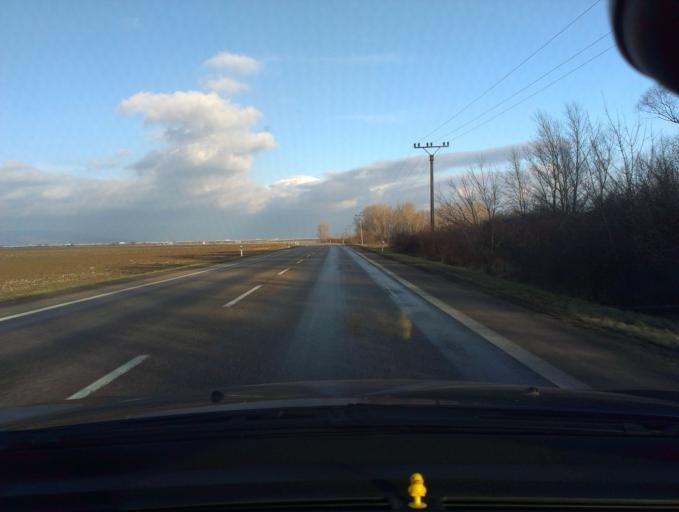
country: SK
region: Trnavsky
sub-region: Okres Trnava
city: Piestany
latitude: 48.6291
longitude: 17.8390
